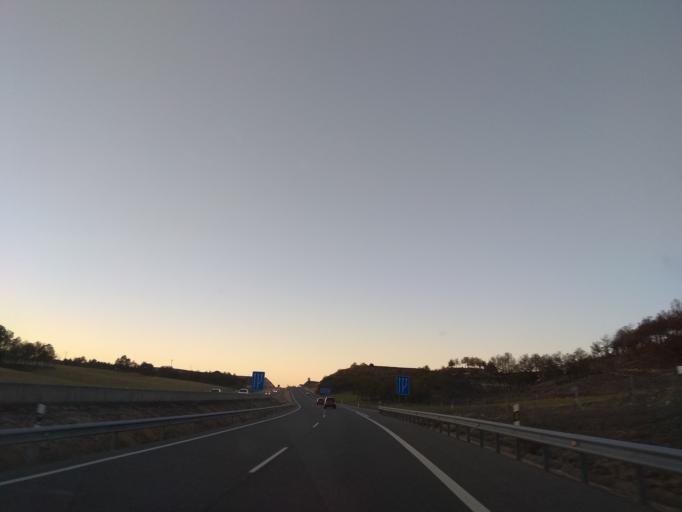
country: ES
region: Castille and Leon
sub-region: Provincia de Burgos
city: Bahabon de Esgueva
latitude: 41.8799
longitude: -3.7326
